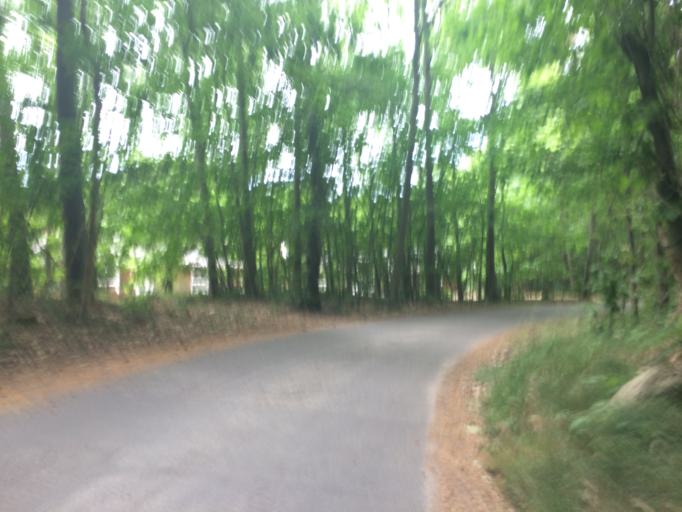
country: DK
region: Capital Region
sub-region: Bornholm Kommune
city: Ronne
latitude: 55.1688
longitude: 14.7175
